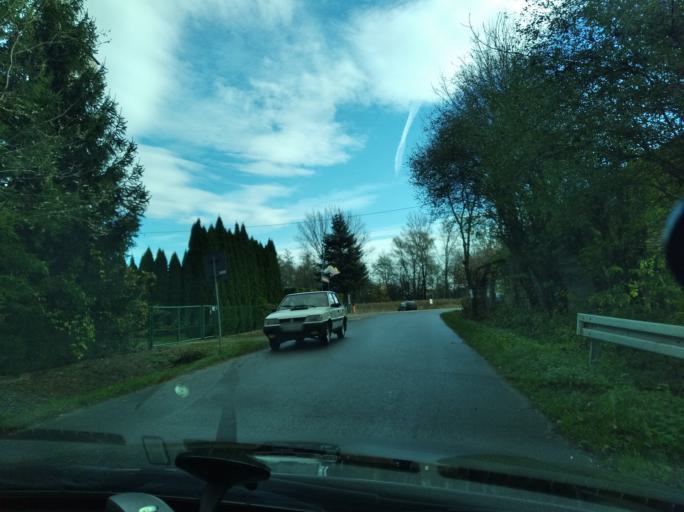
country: PL
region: Subcarpathian Voivodeship
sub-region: Powiat ropczycko-sedziszowski
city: Ostrow
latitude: 50.0965
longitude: 21.5534
